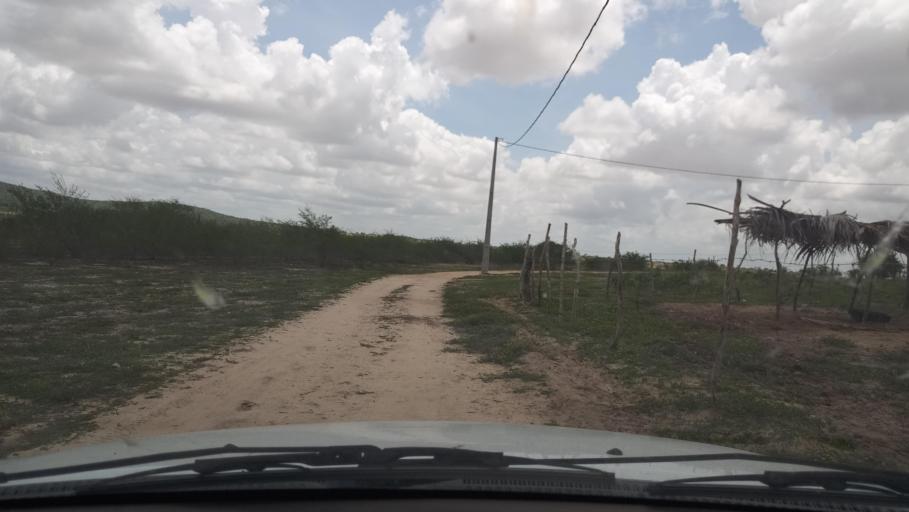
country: BR
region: Rio Grande do Norte
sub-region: Tangara
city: Tangara
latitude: -6.0944
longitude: -35.7087
